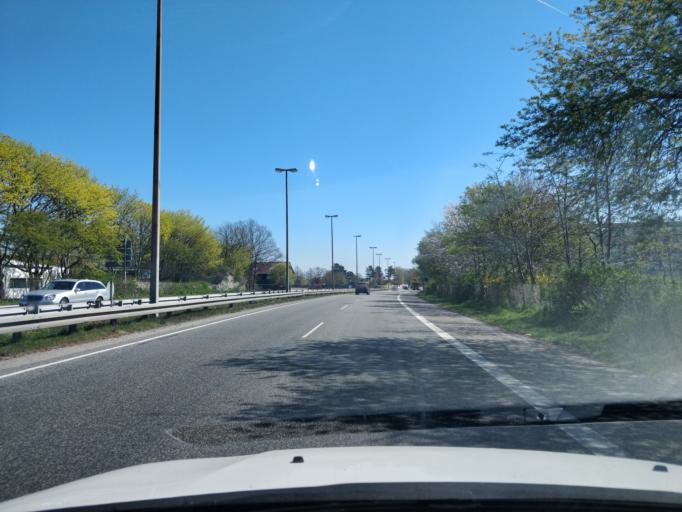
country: DK
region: Capital Region
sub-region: Ishoj Kommune
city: Ishoj
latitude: 55.6137
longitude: 12.3620
